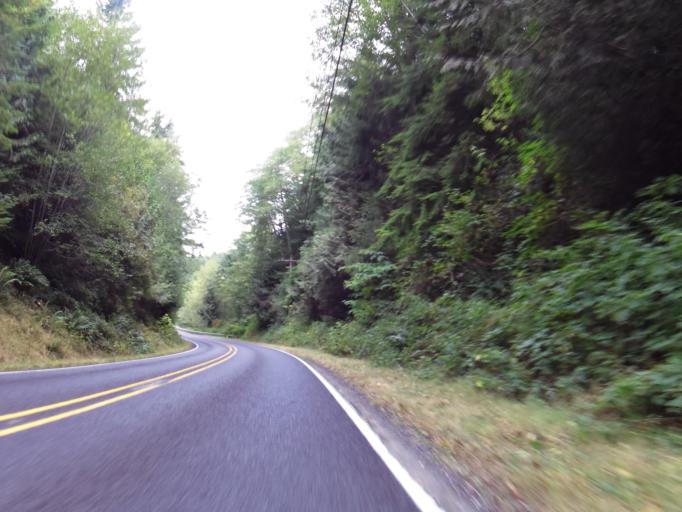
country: US
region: Washington
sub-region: Jefferson County
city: Port Ludlow
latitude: 47.9106
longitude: -122.6768
